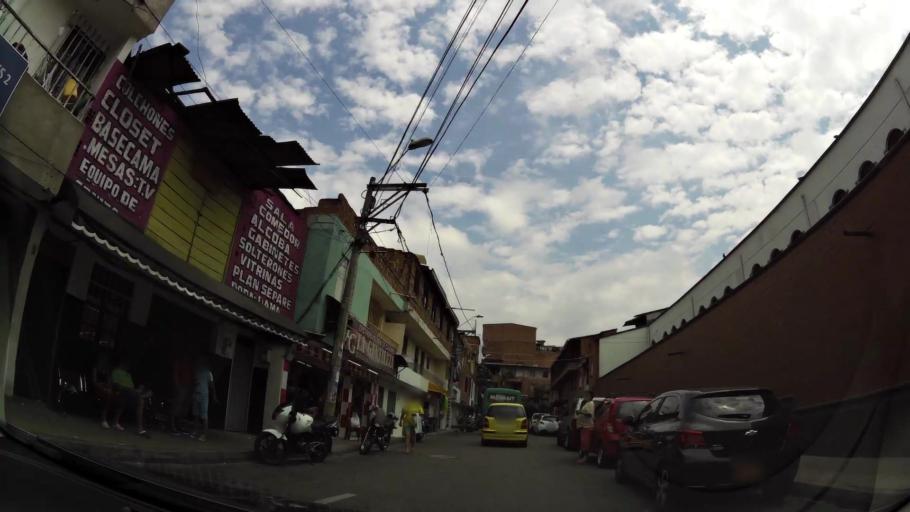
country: CO
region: Antioquia
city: Medellin
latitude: 6.2456
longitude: -75.6207
